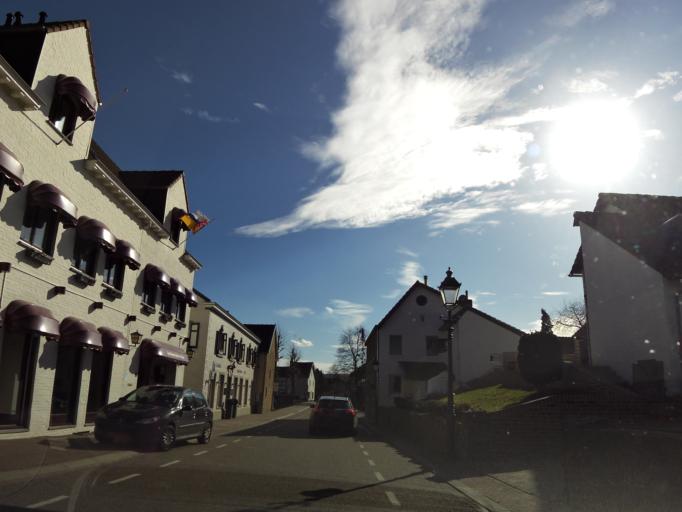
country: BE
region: Wallonia
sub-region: Province de Liege
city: Plombieres
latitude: 50.7760
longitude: 5.9127
